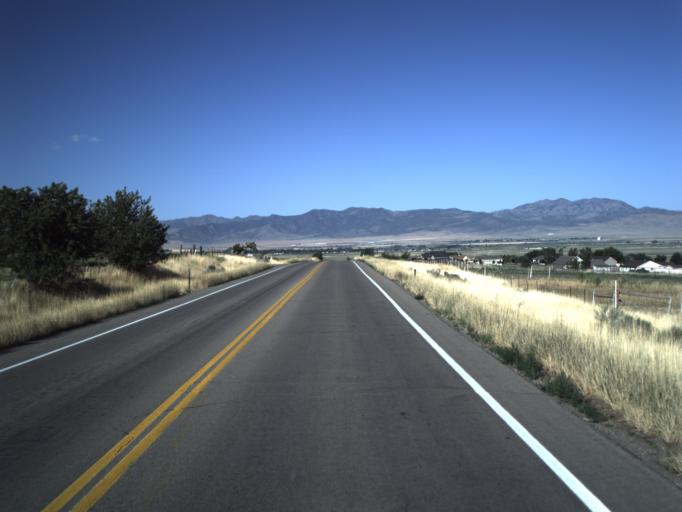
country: US
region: Utah
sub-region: Utah County
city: Genola
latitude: 39.9784
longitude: -111.8388
